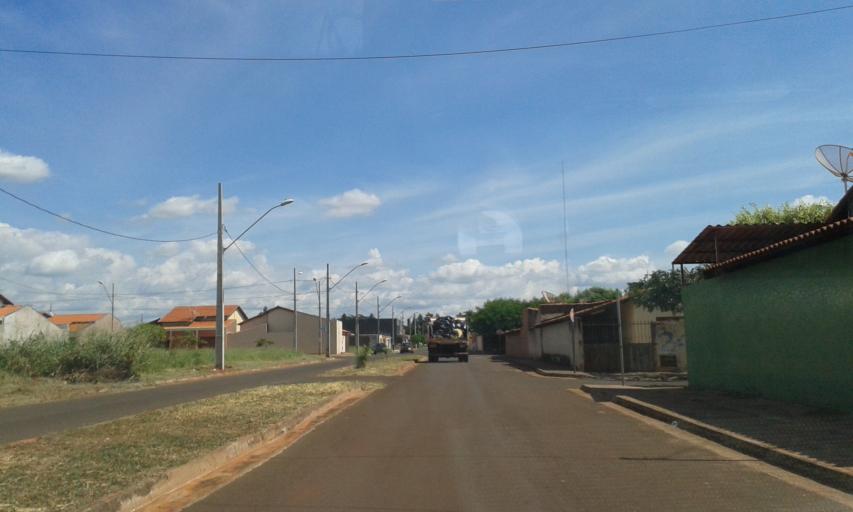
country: BR
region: Minas Gerais
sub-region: Santa Vitoria
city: Santa Vitoria
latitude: -18.8531
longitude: -50.1260
